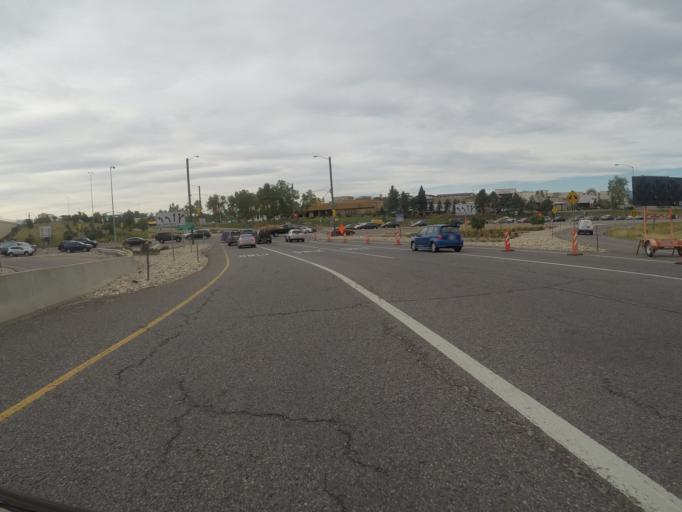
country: US
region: Colorado
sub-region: Arapahoe County
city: Centennial
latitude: 39.5669
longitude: -104.8741
